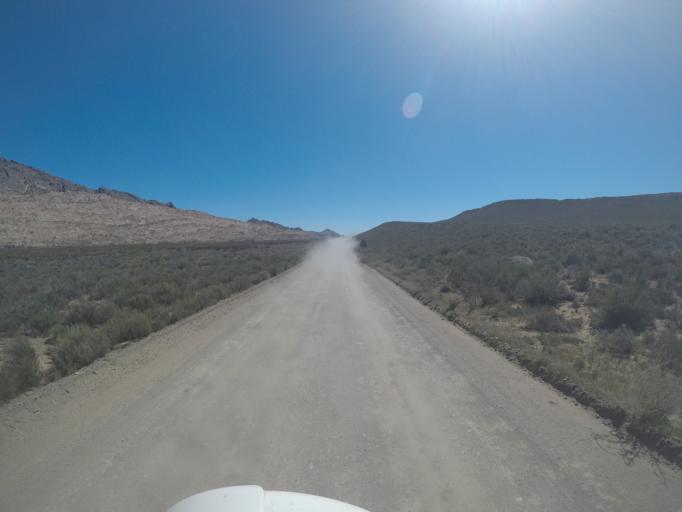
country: ZA
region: Western Cape
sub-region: Cape Winelands District Municipality
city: Ceres
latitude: -32.8264
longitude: 19.4546
